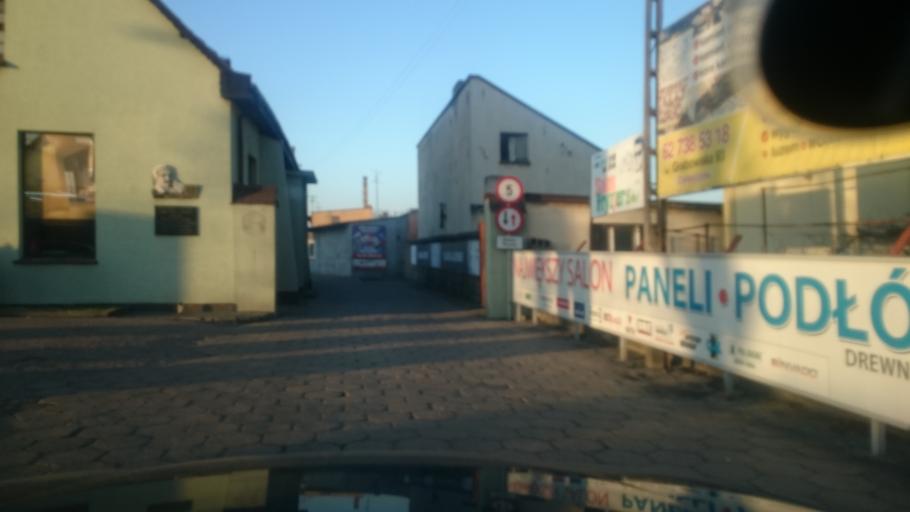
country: PL
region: Greater Poland Voivodeship
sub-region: Powiat ostrowski
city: Ostrow Wielkopolski
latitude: 51.6479
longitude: 17.8491
